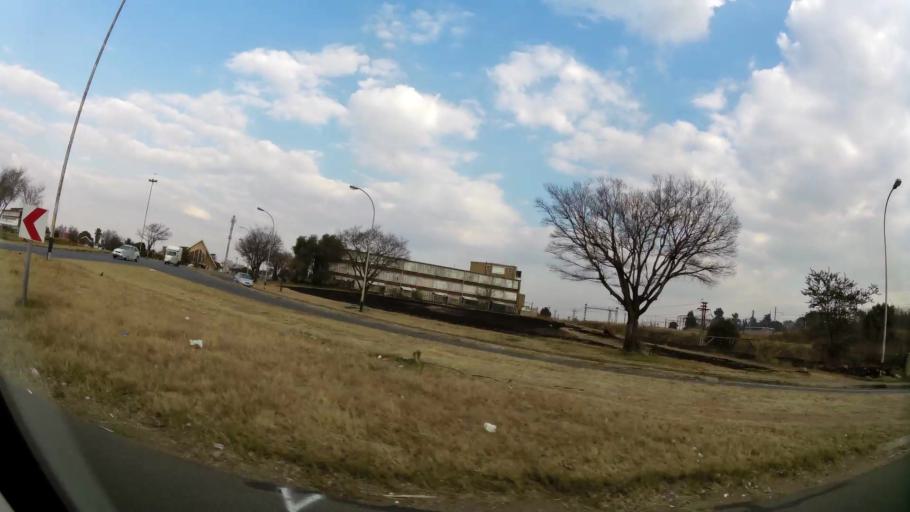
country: ZA
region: Gauteng
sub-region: Ekurhuleni Metropolitan Municipality
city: Germiston
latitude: -26.2366
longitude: 28.1951
